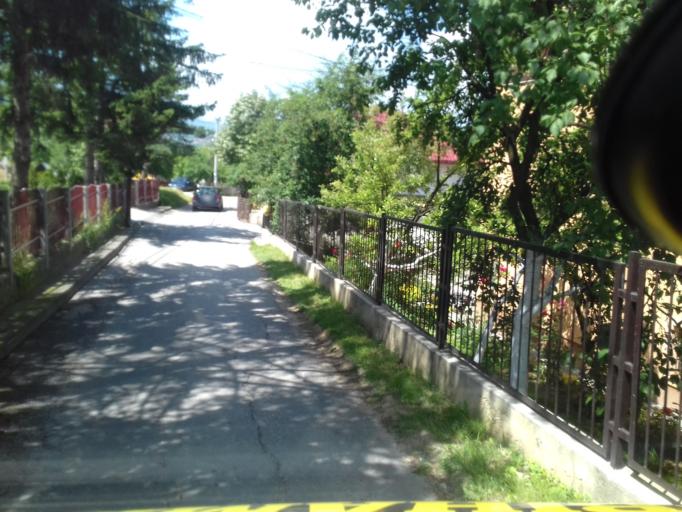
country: BA
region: Federation of Bosnia and Herzegovina
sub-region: Kanton Sarajevo
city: Sarajevo
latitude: 43.8624
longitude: 18.3219
